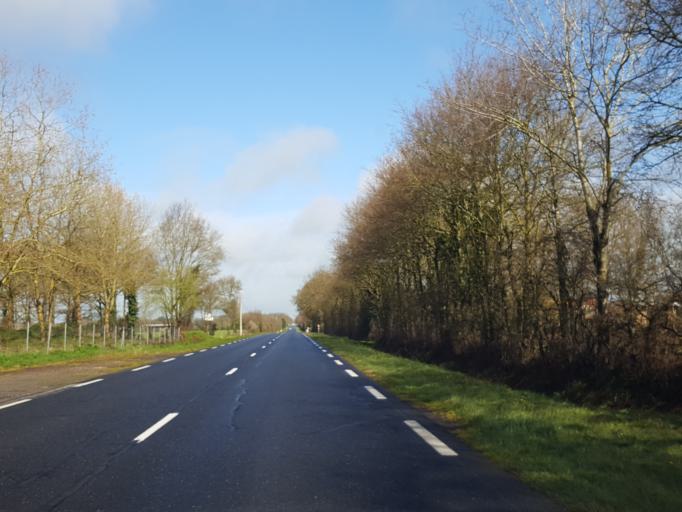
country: FR
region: Pays de la Loire
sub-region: Departement de la Vendee
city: Les Lucs-sur-Boulogne
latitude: 46.8197
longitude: -1.4693
